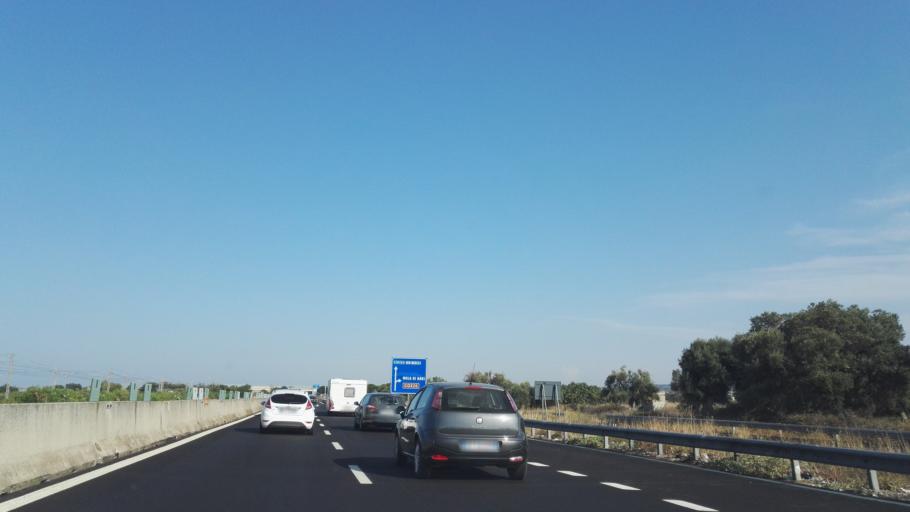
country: IT
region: Apulia
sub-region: Provincia di Bari
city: Mola di Bari
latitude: 41.0468
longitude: 17.1032
